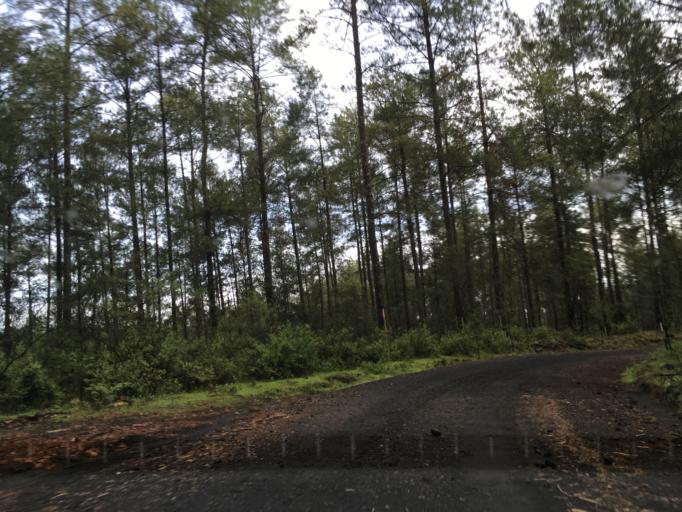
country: MX
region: Michoacan
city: Angahuan
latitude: 19.4915
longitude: -102.2080
